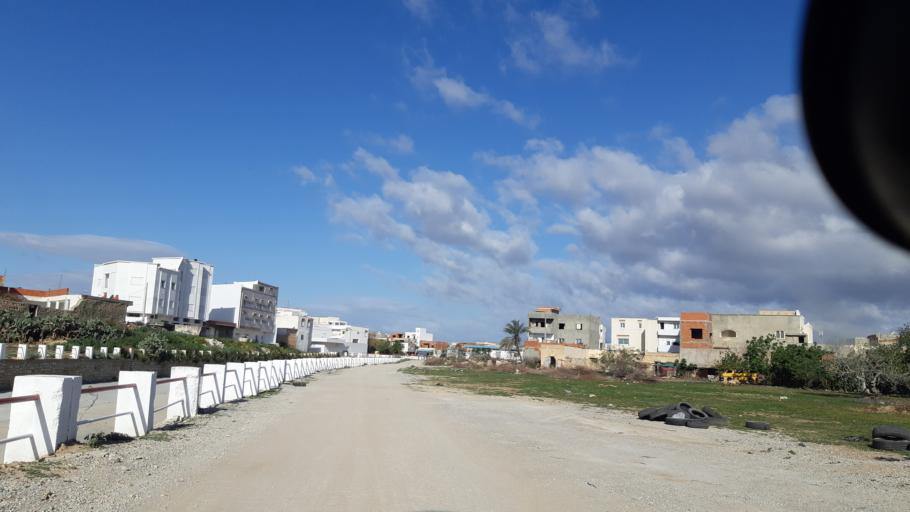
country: TN
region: Susah
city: Akouda
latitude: 35.8712
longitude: 10.5477
